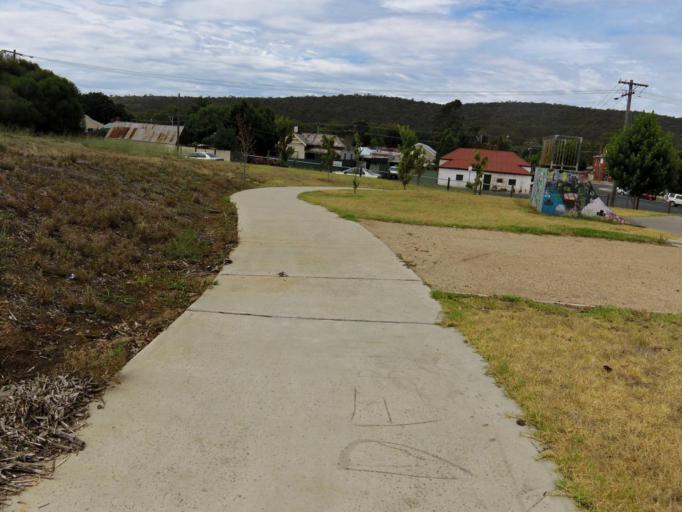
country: AU
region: Victoria
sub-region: Greater Bendigo
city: Kennington
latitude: -36.9247
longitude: 144.7089
